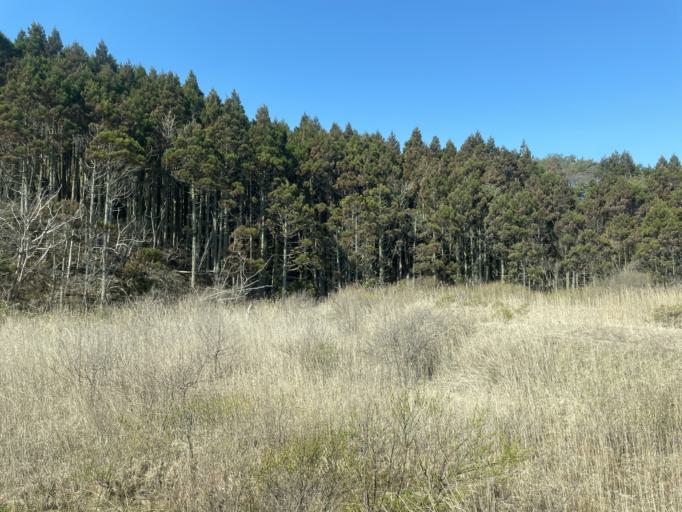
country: JP
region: Aomori
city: Hachinohe
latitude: 40.3222
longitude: 141.7731
